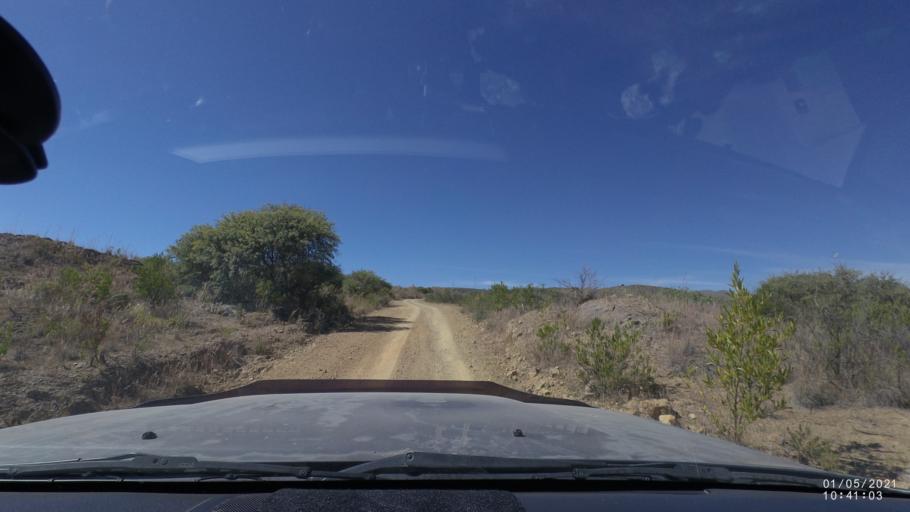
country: BO
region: Cochabamba
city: Capinota
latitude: -17.6068
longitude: -66.1790
